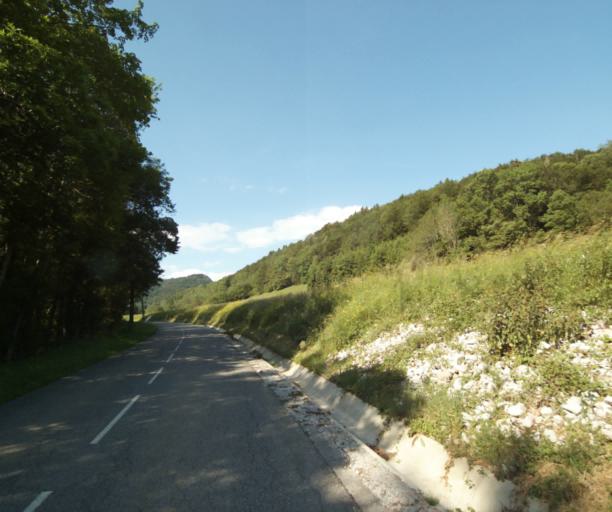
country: FR
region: Rhone-Alpes
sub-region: Departement de la Haute-Savoie
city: Lyaud
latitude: 46.3137
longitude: 6.5045
